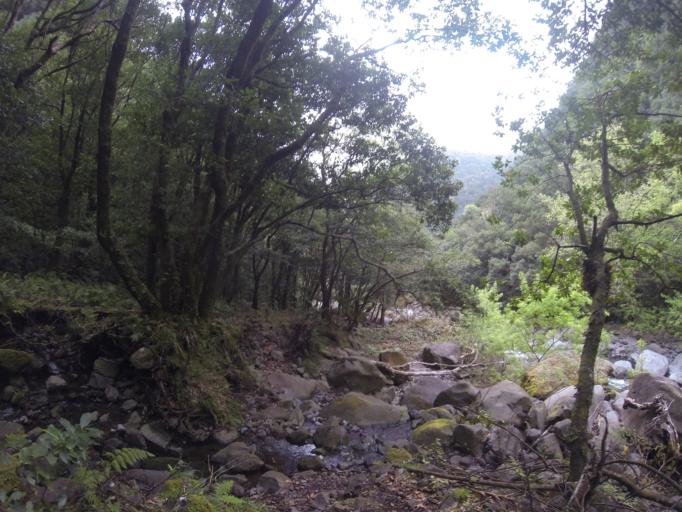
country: PT
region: Madeira
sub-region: Sao Vicente
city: Sao Vicente
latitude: 32.7907
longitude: -17.1144
